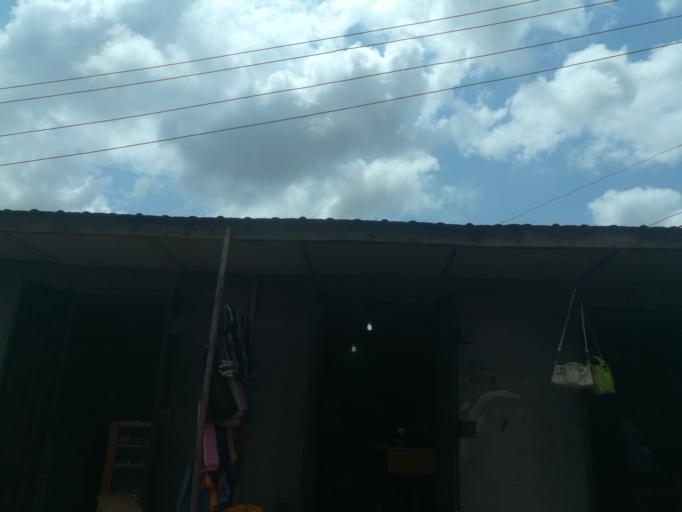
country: NG
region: Oyo
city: Ibadan
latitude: 7.3665
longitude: 3.8183
